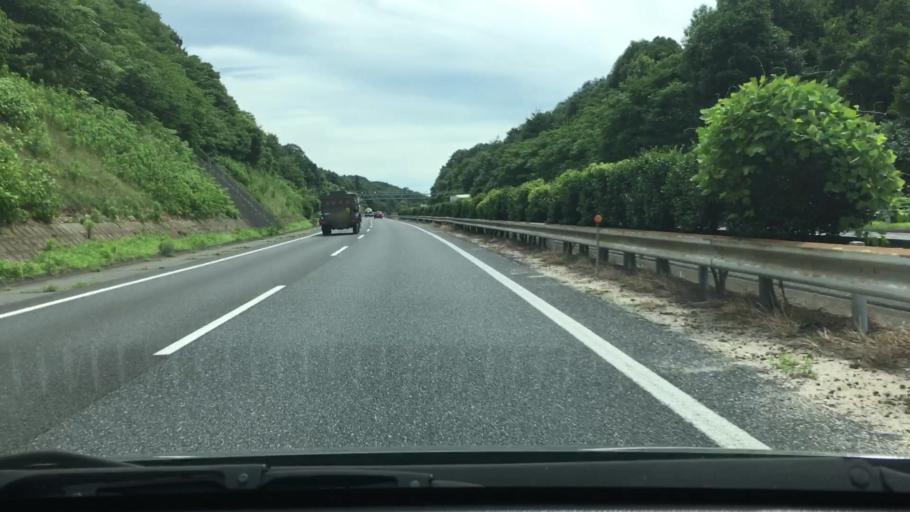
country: JP
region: Yamaguchi
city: Yanai
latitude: 34.0761
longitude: 132.0694
